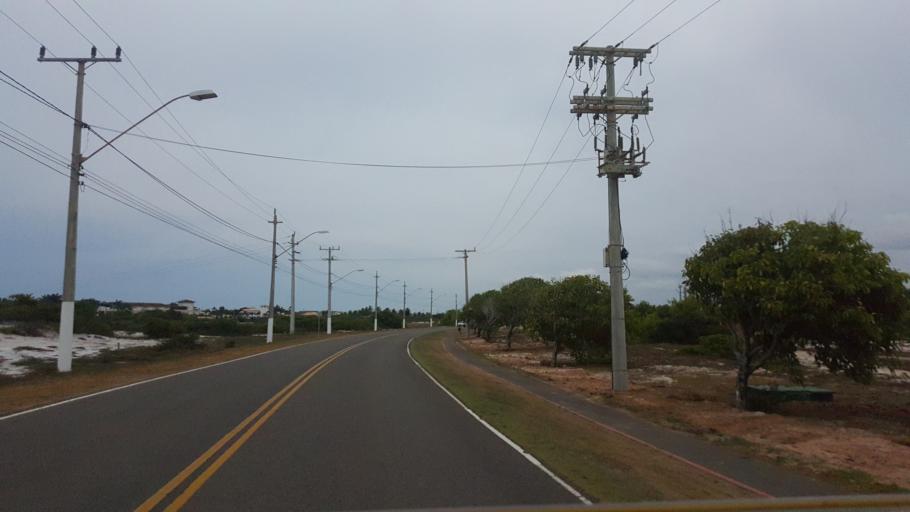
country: BR
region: Bahia
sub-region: Mata De Sao Joao
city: Mata de Sao Joao
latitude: -12.4350
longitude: -37.9203
